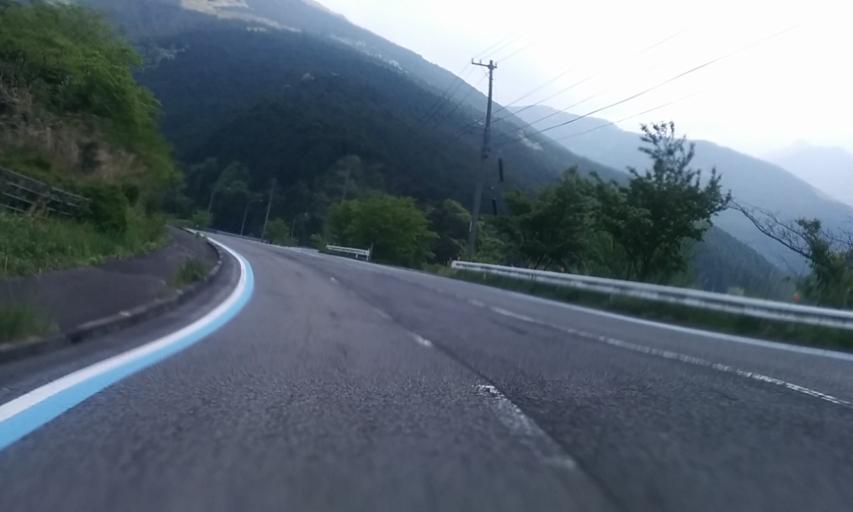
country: JP
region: Ehime
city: Saijo
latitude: 33.8319
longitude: 133.2307
